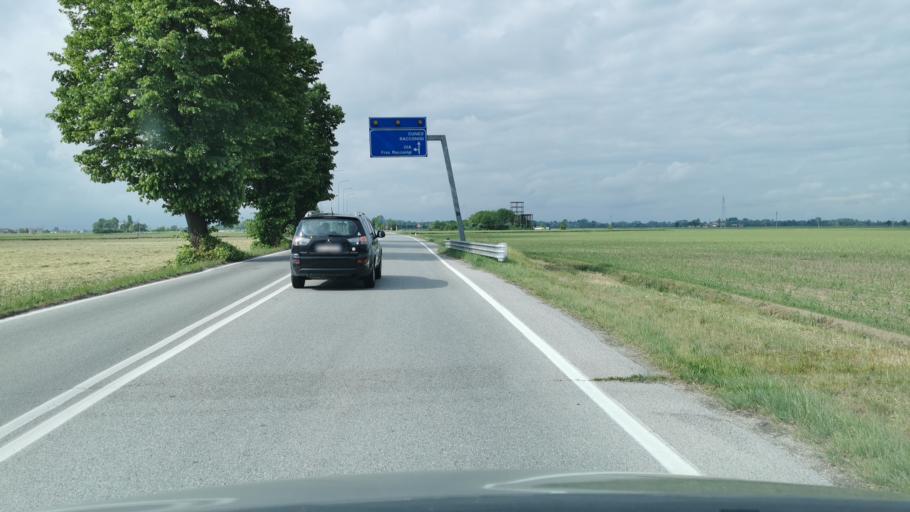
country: IT
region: Piedmont
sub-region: Provincia di Cuneo
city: Racconigi
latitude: 44.8072
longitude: 7.6956
